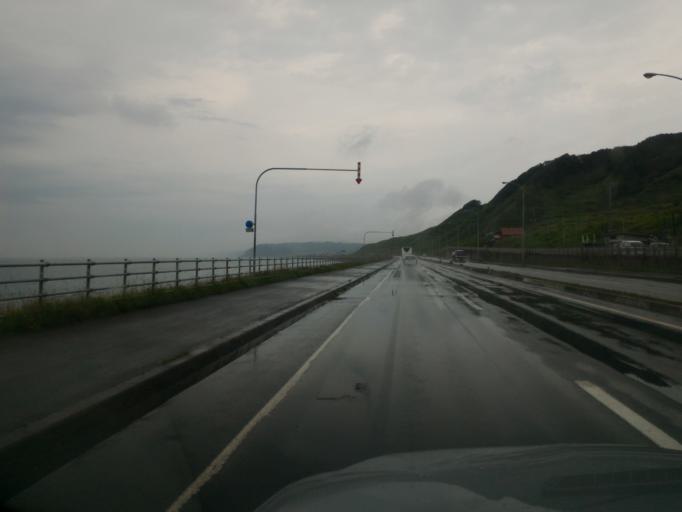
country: JP
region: Hokkaido
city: Rumoi
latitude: 44.0021
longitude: 141.6576
